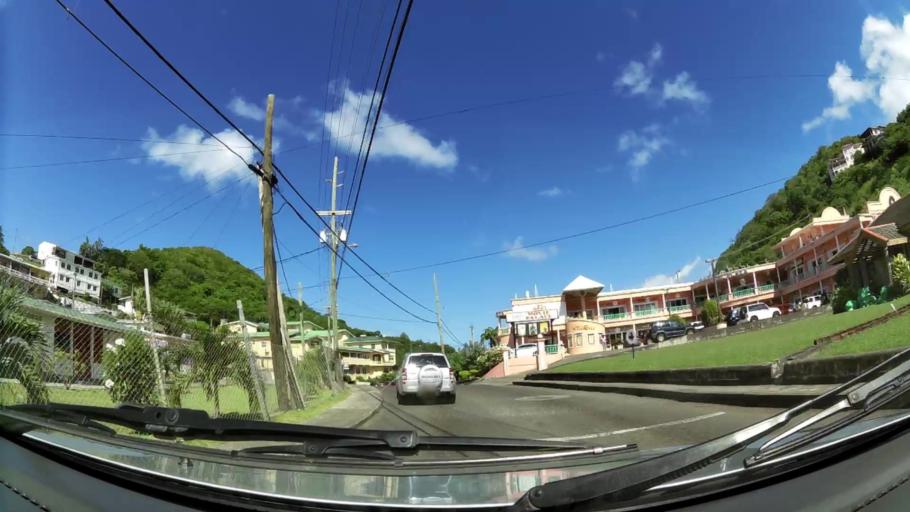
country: GD
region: Saint George
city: Saint George's
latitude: 12.0179
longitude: -61.7587
